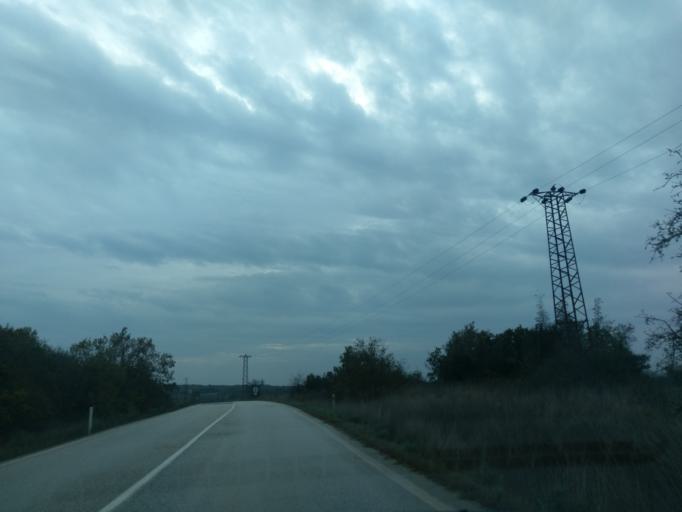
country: TR
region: Istanbul
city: Canta
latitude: 41.1740
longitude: 28.0913
